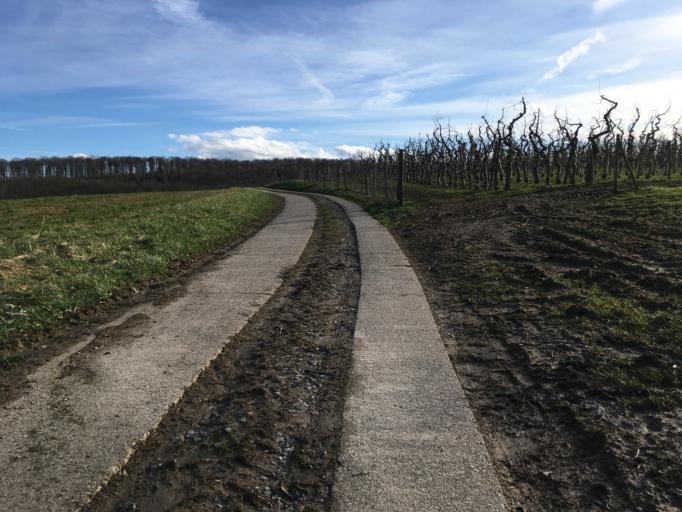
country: DE
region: Baden-Wuerttemberg
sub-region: Regierungsbezirk Stuttgart
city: Lehrensteinsfeld
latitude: 49.1294
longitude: 9.3369
